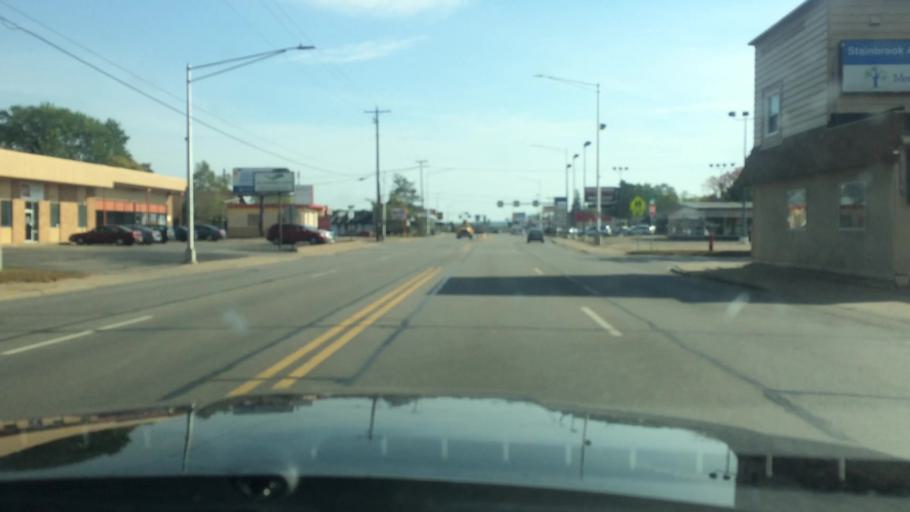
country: US
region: Wisconsin
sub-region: Marathon County
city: Wausau
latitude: 44.9365
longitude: -89.6174
